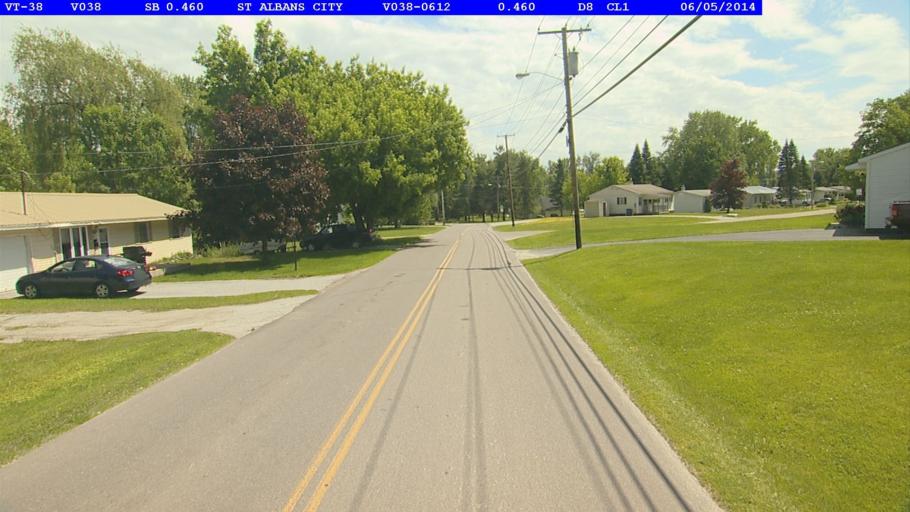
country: US
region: Vermont
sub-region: Franklin County
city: Saint Albans
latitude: 44.8232
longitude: -73.0887
